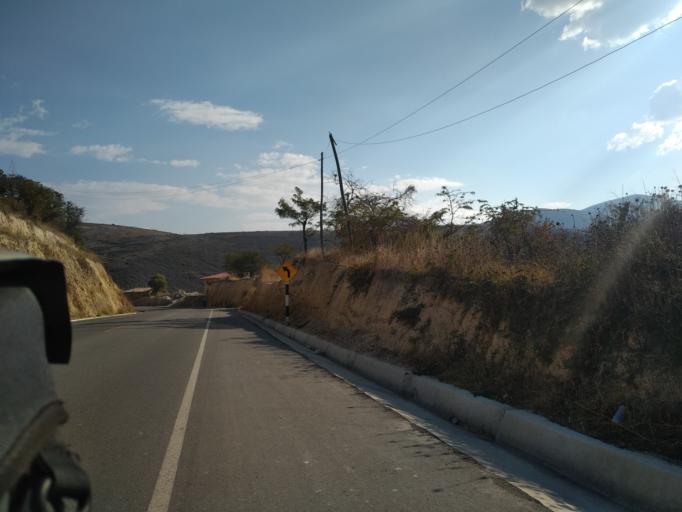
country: PE
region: Cajamarca
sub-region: San Marcos
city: San Marcos
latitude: -7.3701
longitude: -78.1286
